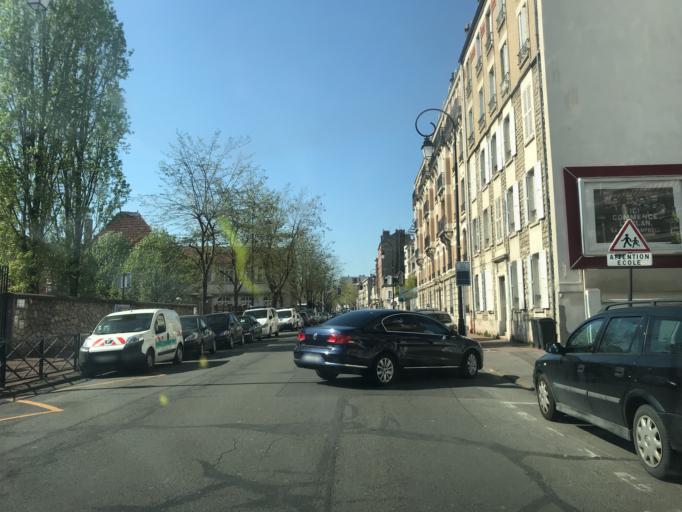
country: FR
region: Ile-de-France
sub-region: Departement du Val-de-Marne
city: Joinville-le-Pont
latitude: 48.8083
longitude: 2.4733
